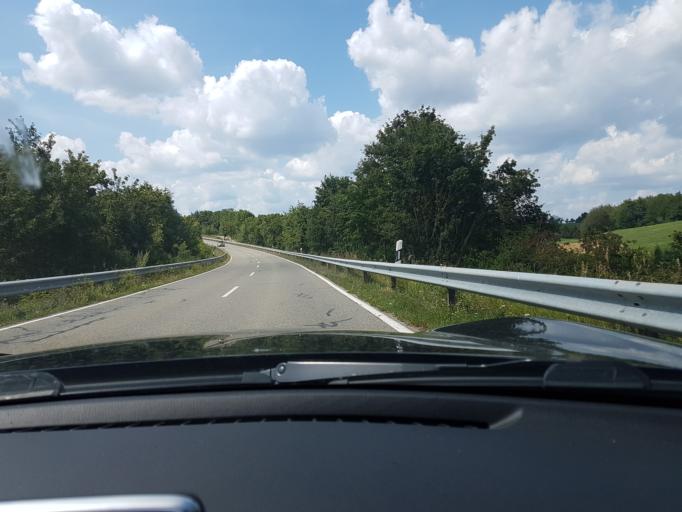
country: DE
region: Baden-Wuerttemberg
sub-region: Karlsruhe Region
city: Limbach
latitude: 49.4258
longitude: 9.2528
